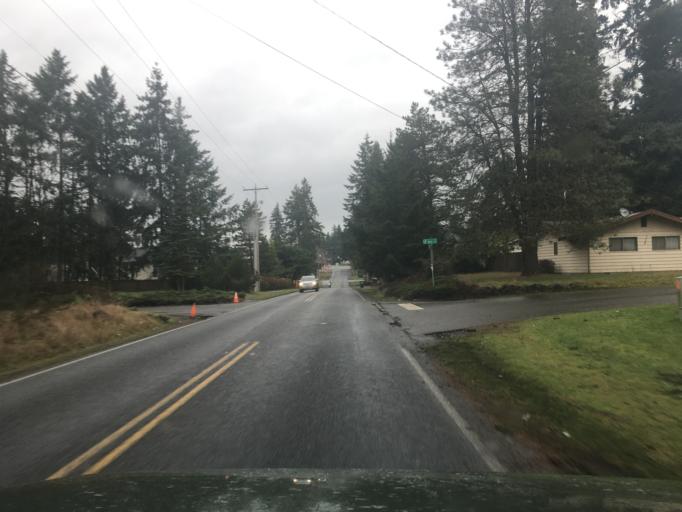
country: US
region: Washington
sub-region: Thurston County
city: Tanglewilde-Thompson Place
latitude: 47.0481
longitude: -122.7913
